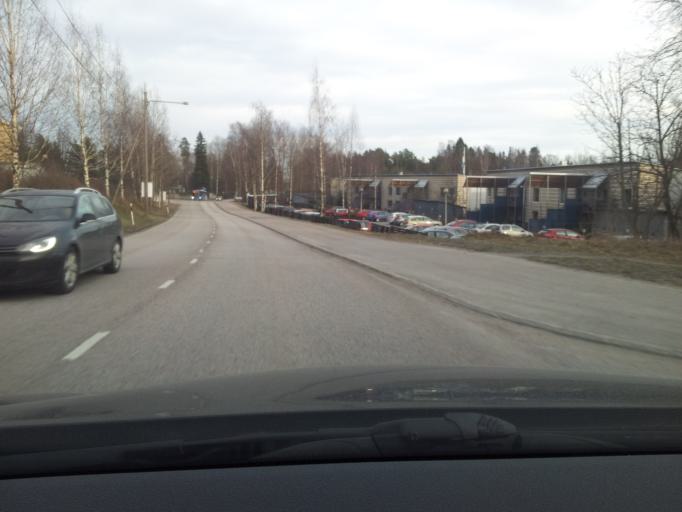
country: FI
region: Uusimaa
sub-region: Helsinki
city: Espoo
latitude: 60.1703
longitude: 24.6902
